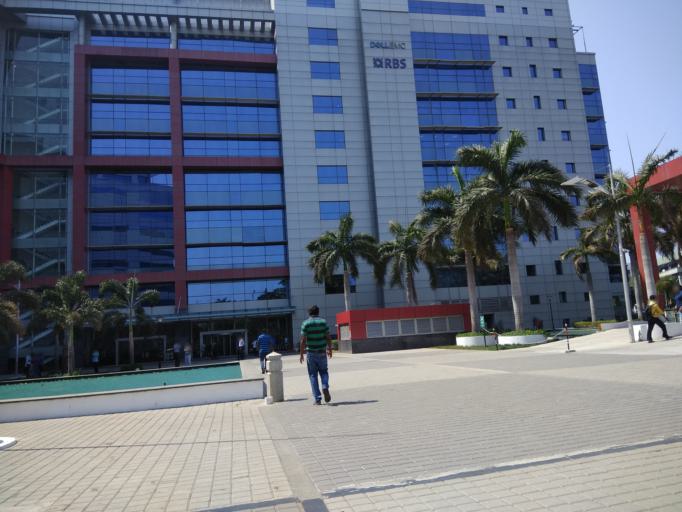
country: IN
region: Tamil Nadu
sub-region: Kancheepuram
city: Alandur
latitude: 13.0147
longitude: 80.2040
